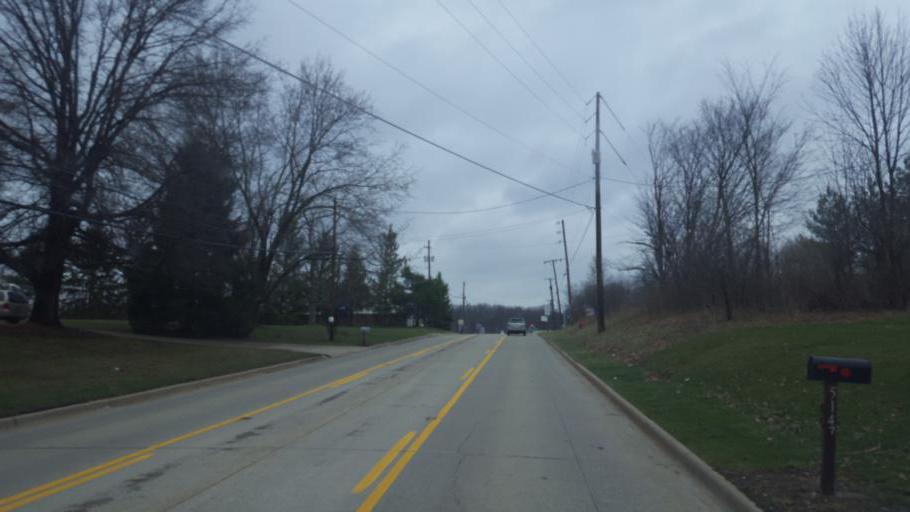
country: US
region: Ohio
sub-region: Medina County
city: Medina
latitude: 41.1346
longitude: -81.8122
